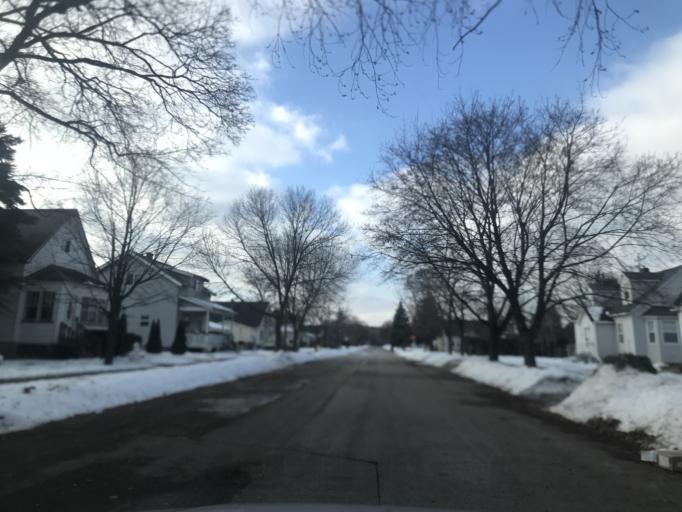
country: US
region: Wisconsin
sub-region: Marinette County
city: Marinette
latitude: 45.1012
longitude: -87.6434
